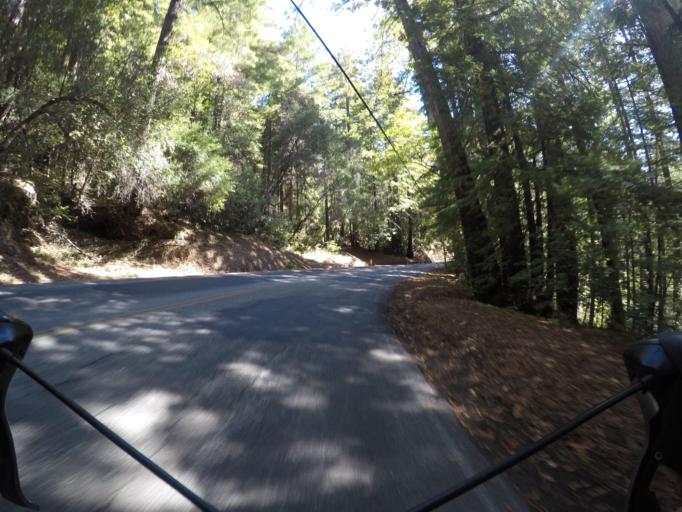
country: US
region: California
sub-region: San Mateo County
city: Portola Valley
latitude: 37.2757
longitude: -122.2991
